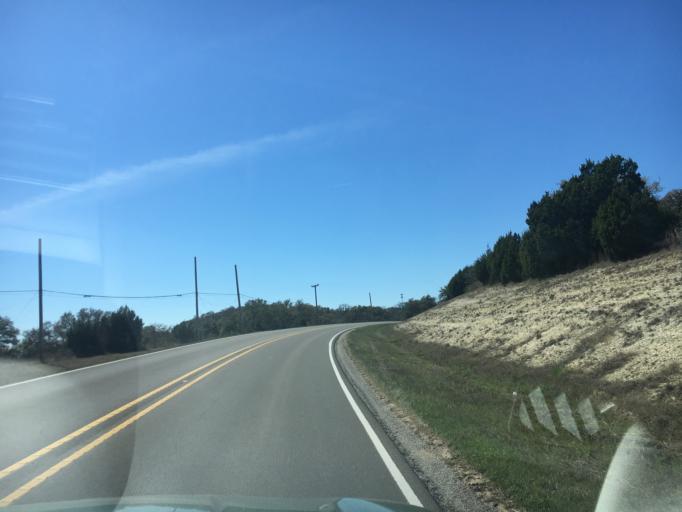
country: US
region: Texas
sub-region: Travis County
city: The Hills
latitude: 30.2967
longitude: -98.0084
